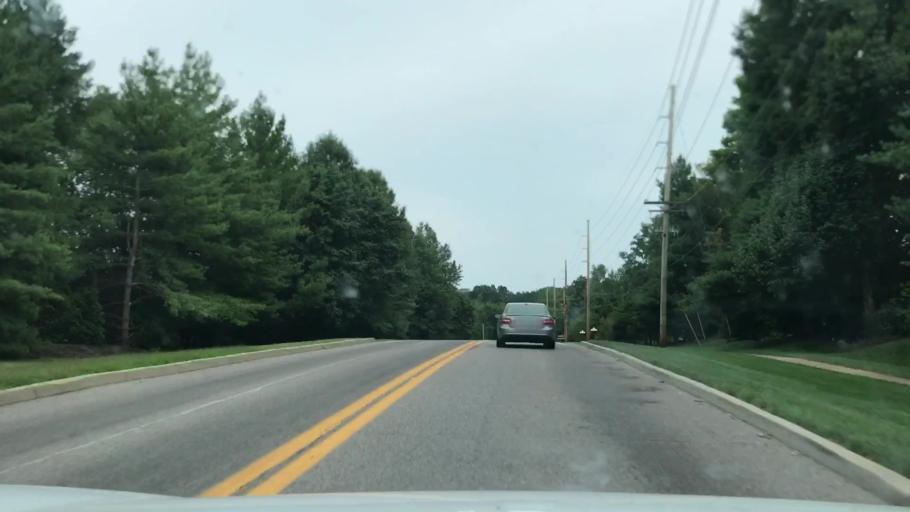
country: US
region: Missouri
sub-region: Saint Louis County
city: Chesterfield
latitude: 38.6548
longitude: -90.6178
